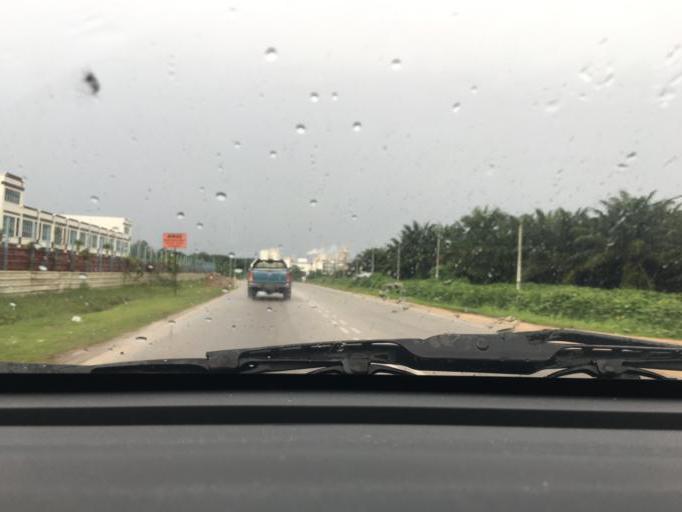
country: MY
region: Kedah
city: Sungai Petani
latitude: 5.6063
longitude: 100.6399
